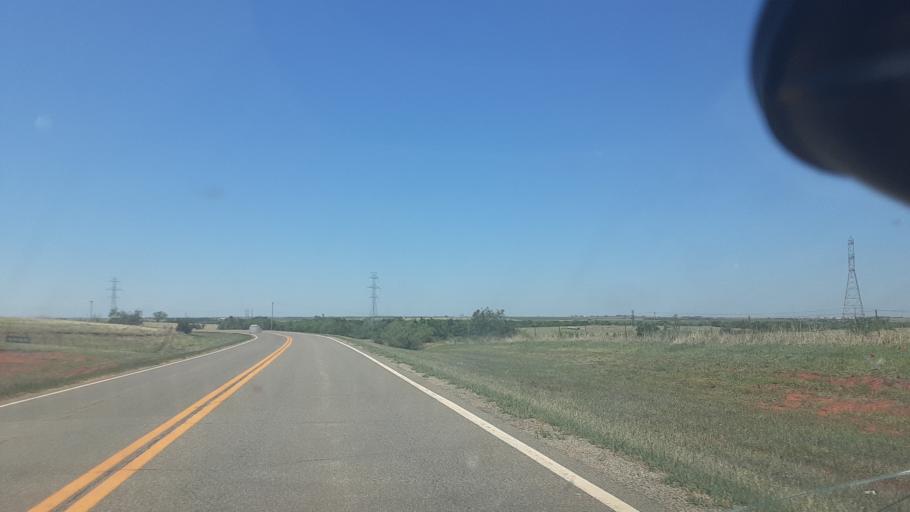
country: US
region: Oklahoma
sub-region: Noble County
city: Perry
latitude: 36.1158
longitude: -97.3682
